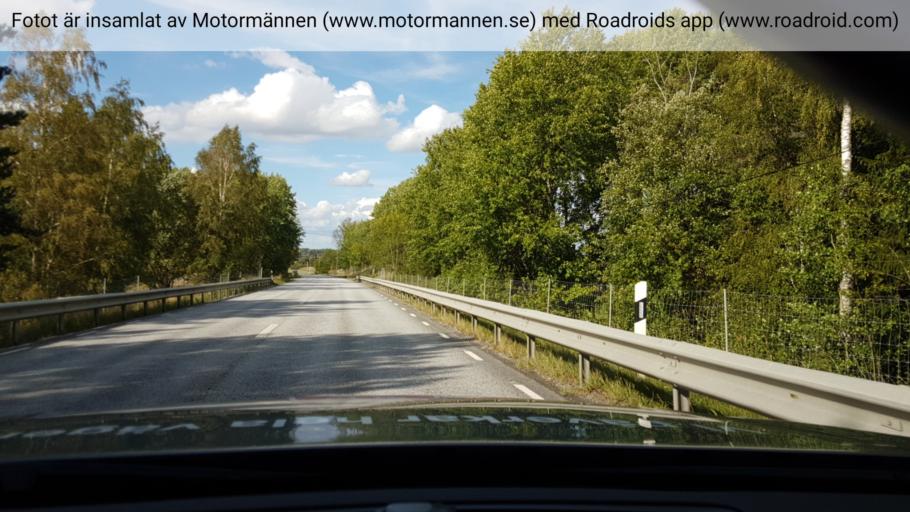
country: SE
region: Uppsala
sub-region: Habo Kommun
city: Balsta
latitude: 59.6090
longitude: 17.6073
